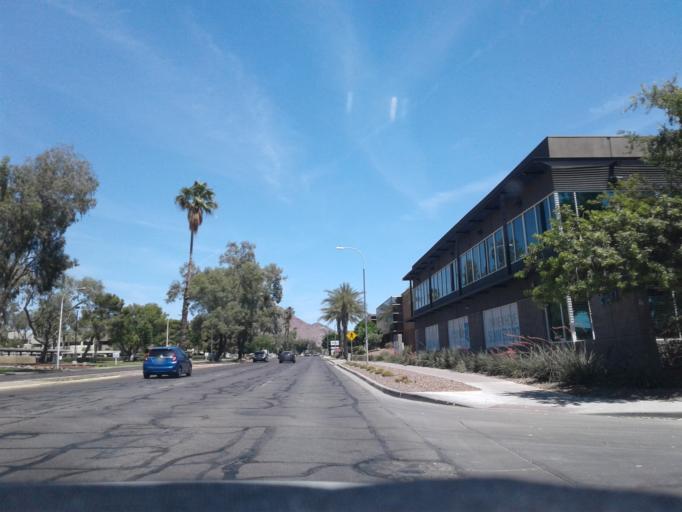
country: US
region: Arizona
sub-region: Maricopa County
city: Paradise Valley
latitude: 33.5096
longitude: -112.0196
